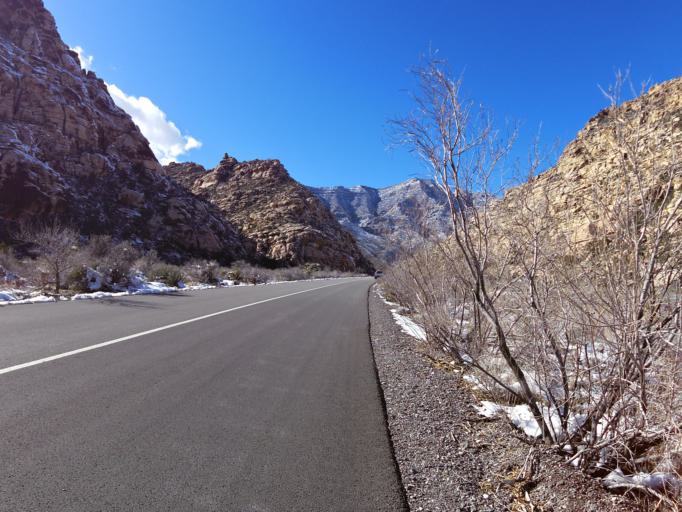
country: US
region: Nevada
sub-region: Clark County
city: Summerlin South
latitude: 36.1584
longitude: -115.4956
